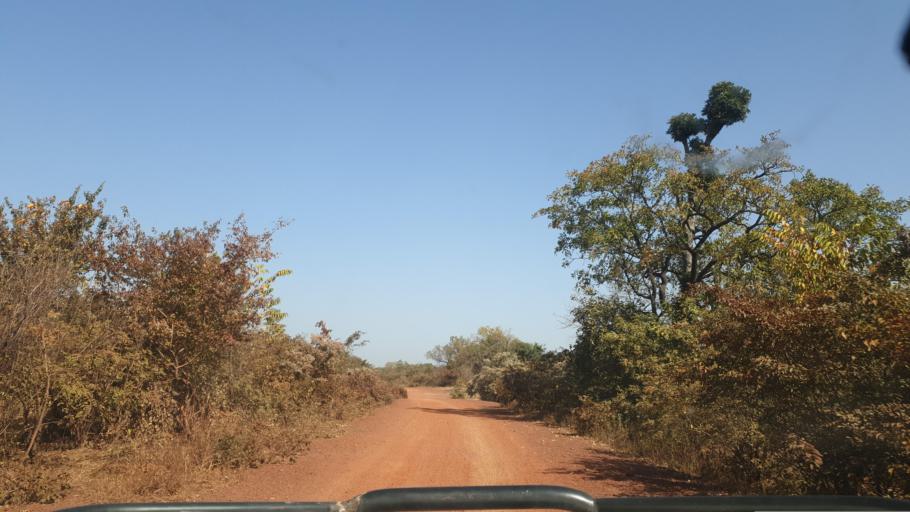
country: ML
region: Sikasso
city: Bougouni
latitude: 11.8301
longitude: -6.9787
